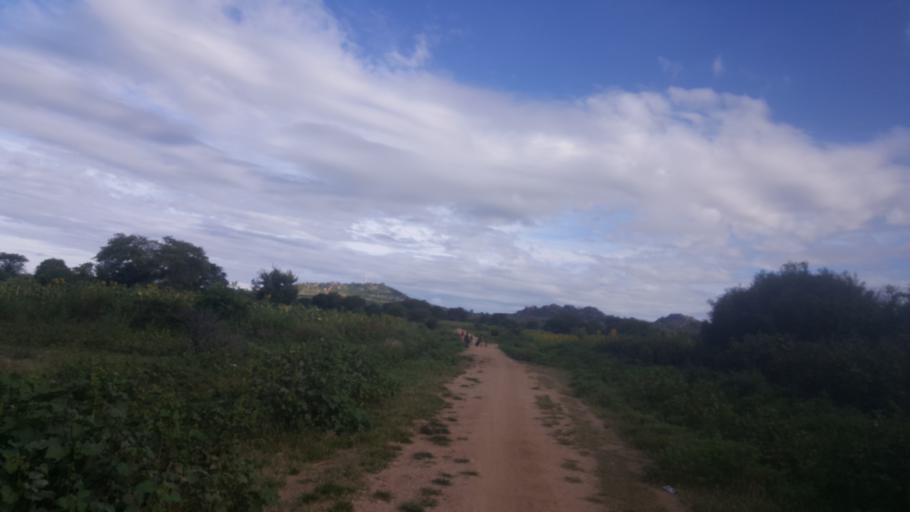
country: TZ
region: Dodoma
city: Dodoma
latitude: -6.0883
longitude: 35.5242
